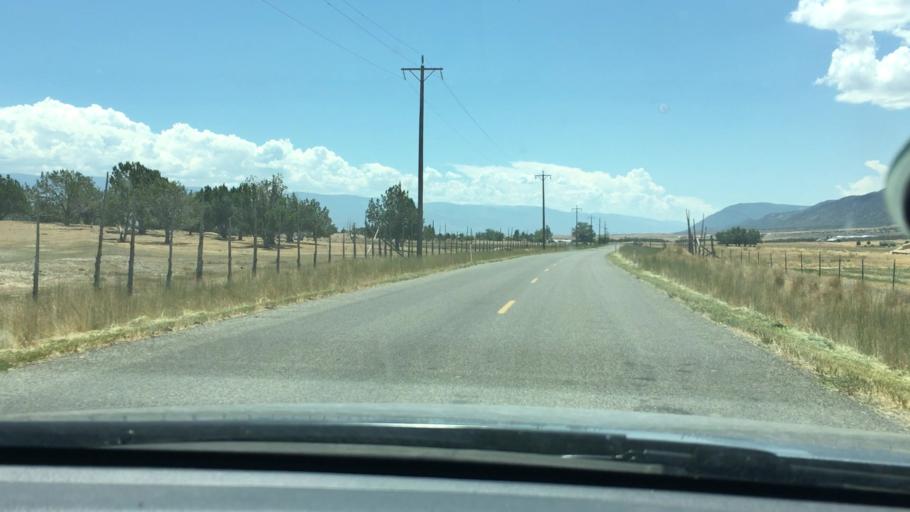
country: US
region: Utah
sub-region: Sanpete County
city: Fountain Green
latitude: 39.6072
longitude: -111.6439
